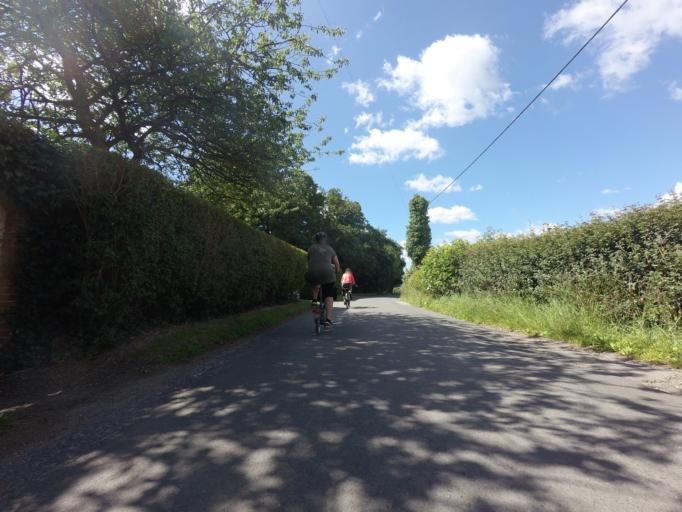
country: GB
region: England
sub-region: East Sussex
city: Horam
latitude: 50.9066
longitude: 0.1948
